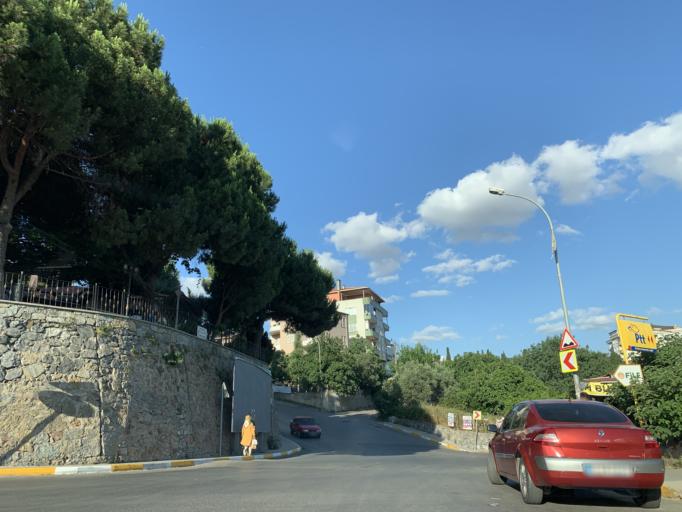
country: TR
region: Istanbul
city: Pendik
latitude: 40.9019
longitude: 29.2576
